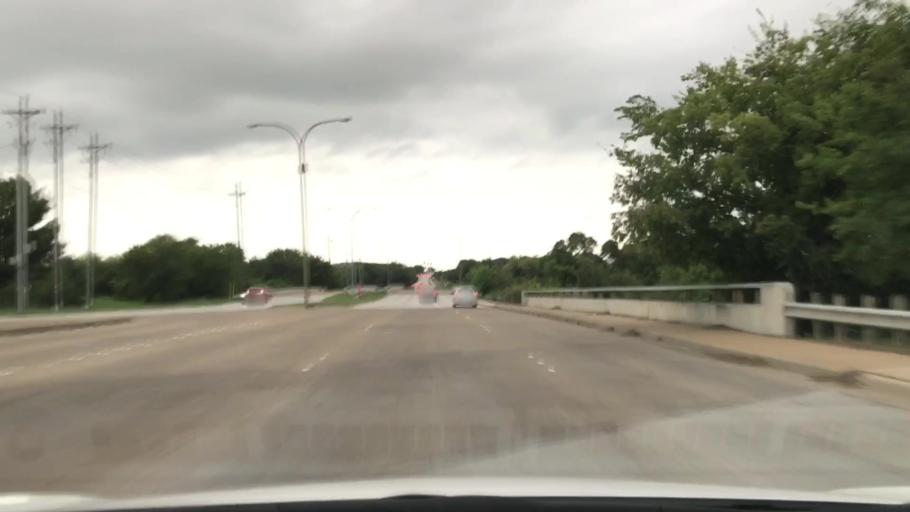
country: US
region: Texas
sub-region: Tarrant County
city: Watauga
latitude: 32.8553
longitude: -97.2901
